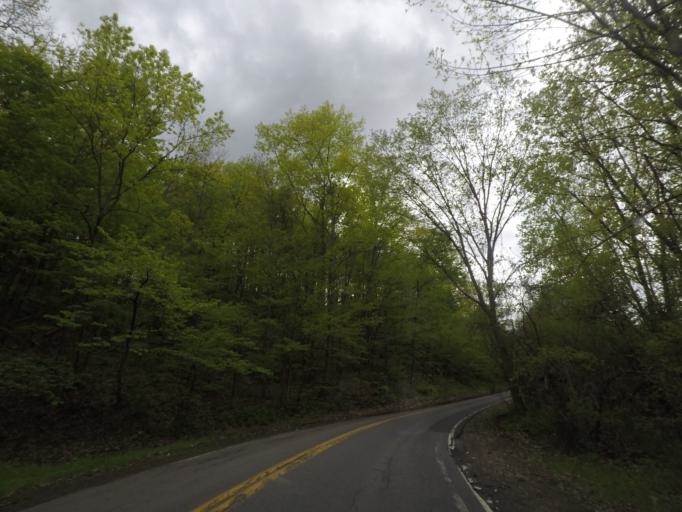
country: US
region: New York
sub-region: Albany County
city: Voorheesville
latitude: 42.6899
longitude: -73.9225
